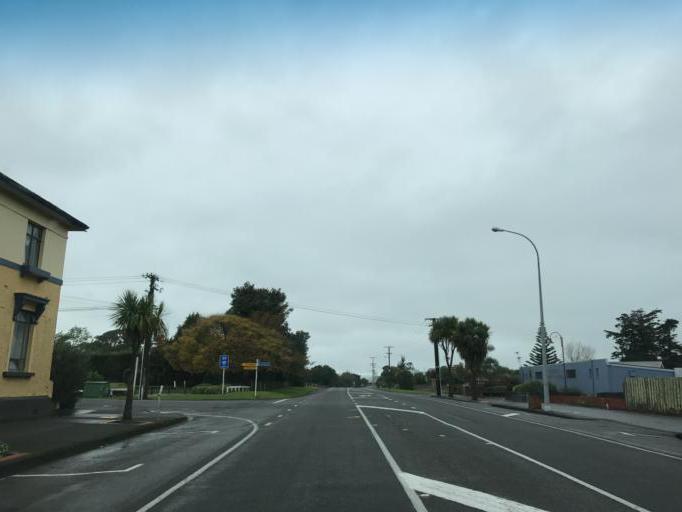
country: NZ
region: Taranaki
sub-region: South Taranaki District
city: Patea
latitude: -39.7639
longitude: 174.6350
